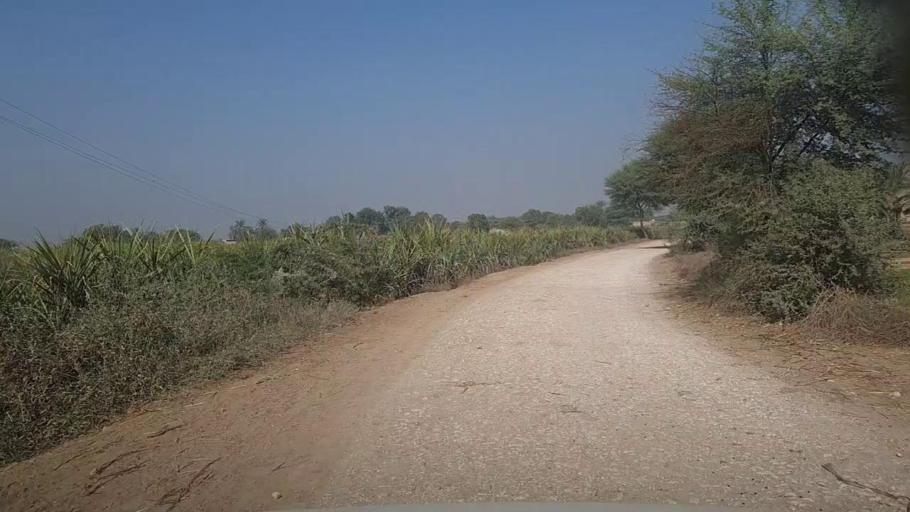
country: PK
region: Sindh
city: Karaundi
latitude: 26.9749
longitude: 68.4502
